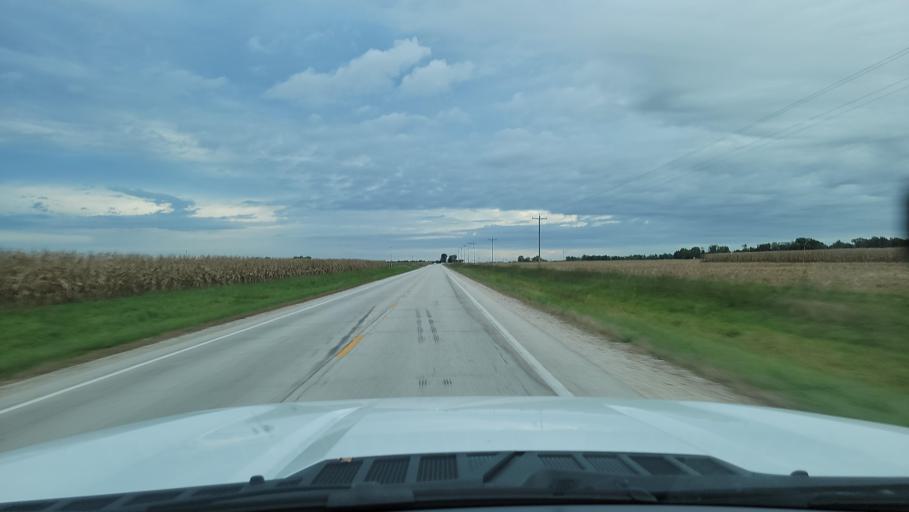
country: US
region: Illinois
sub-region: Schuyler County
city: Rushville
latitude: 40.0690
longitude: -90.6151
